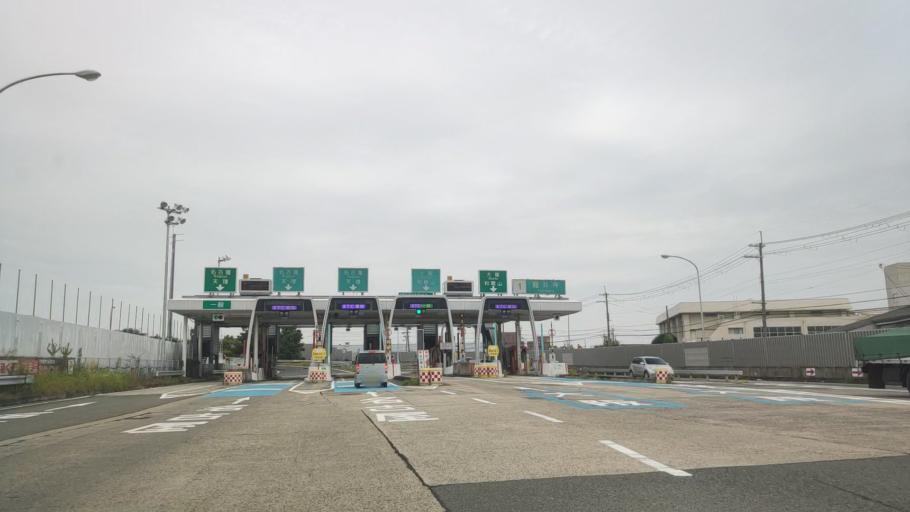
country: JP
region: Osaka
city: Kashihara
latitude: 34.5744
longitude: 135.6038
